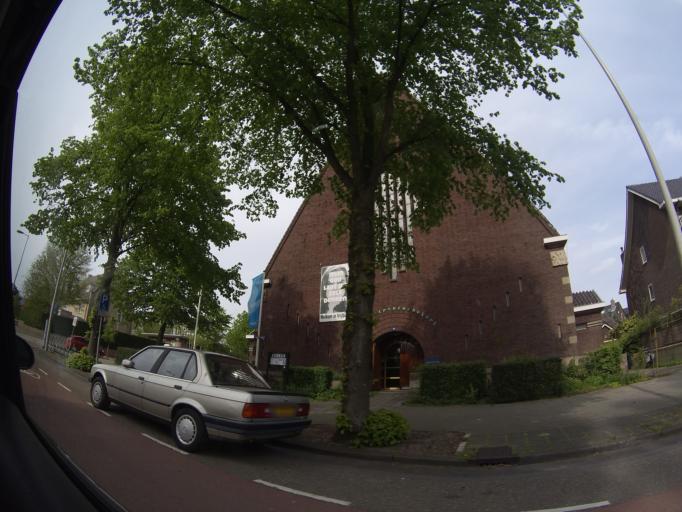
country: NL
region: North Holland
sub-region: Gemeente Amsterdam
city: Amsterdam
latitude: 52.3456
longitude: 4.8823
